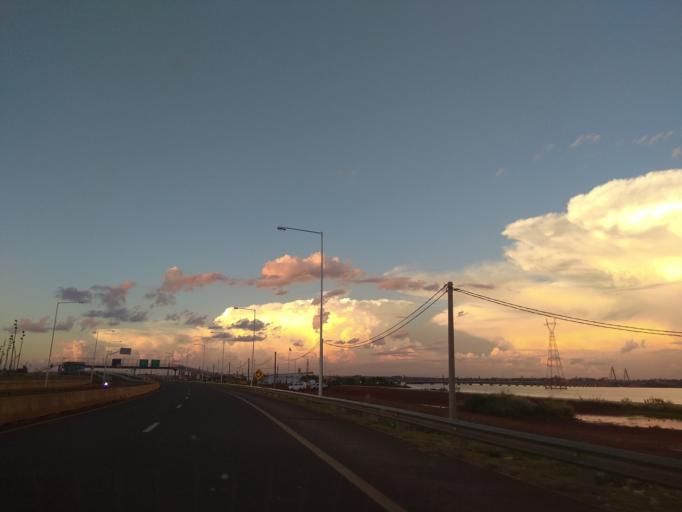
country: AR
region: Misiones
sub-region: Departamento de Capital
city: Posadas
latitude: -27.3825
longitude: -55.8850
